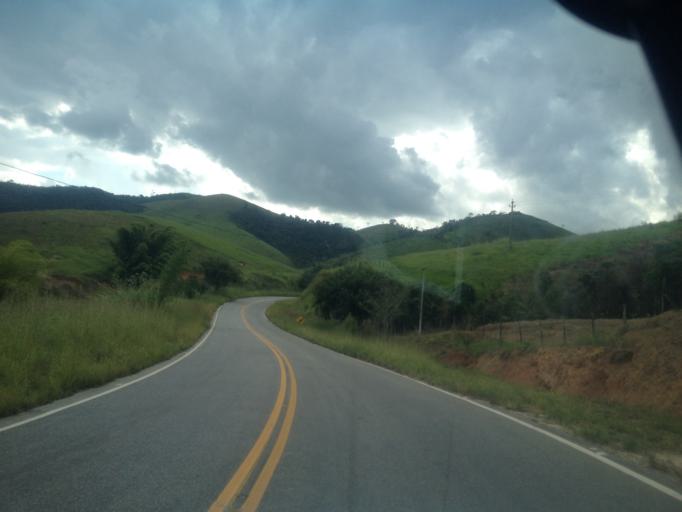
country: BR
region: Rio de Janeiro
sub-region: Quatis
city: Quatis
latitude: -22.3921
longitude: -44.2641
